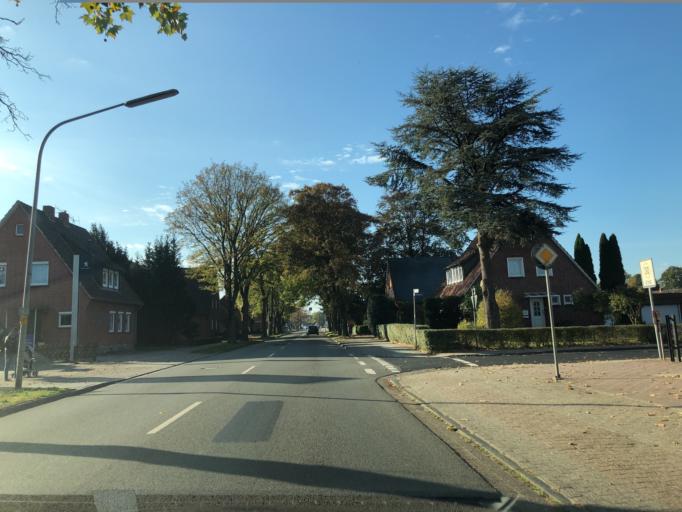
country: DE
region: Lower Saxony
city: Papenburg
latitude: 53.0754
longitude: 7.4258
